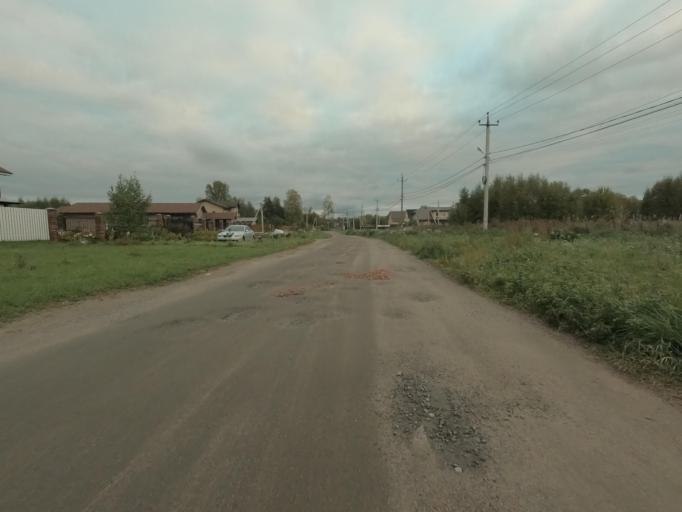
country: RU
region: Leningrad
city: Pavlovo
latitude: 59.8113
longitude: 30.9180
